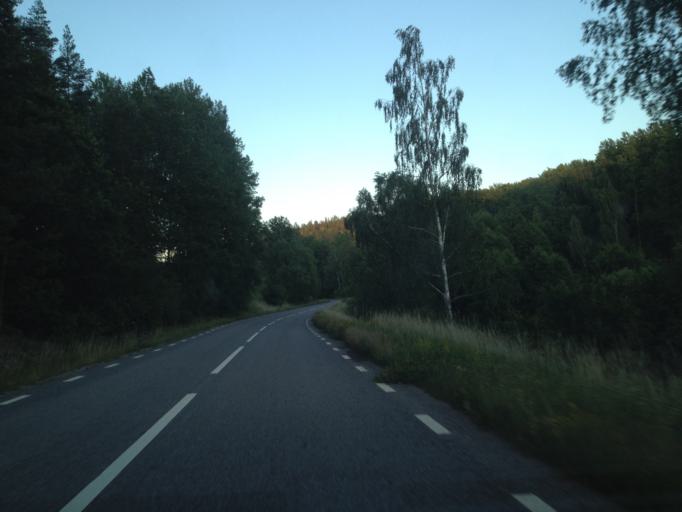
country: SE
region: Kalmar
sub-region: Vasterviks Kommun
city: Overum
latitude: 58.0221
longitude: 16.1298
